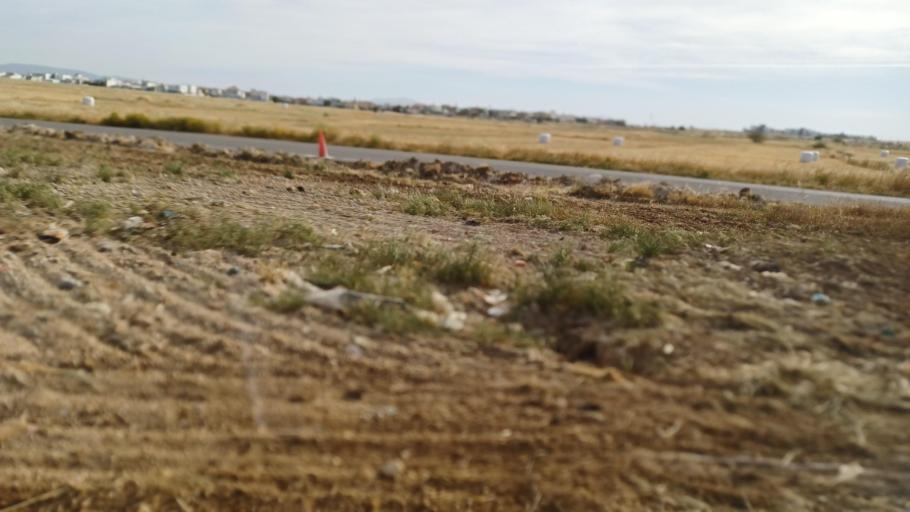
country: CY
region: Lefkosia
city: Kokkinotrimithia
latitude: 35.1629
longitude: 33.1942
